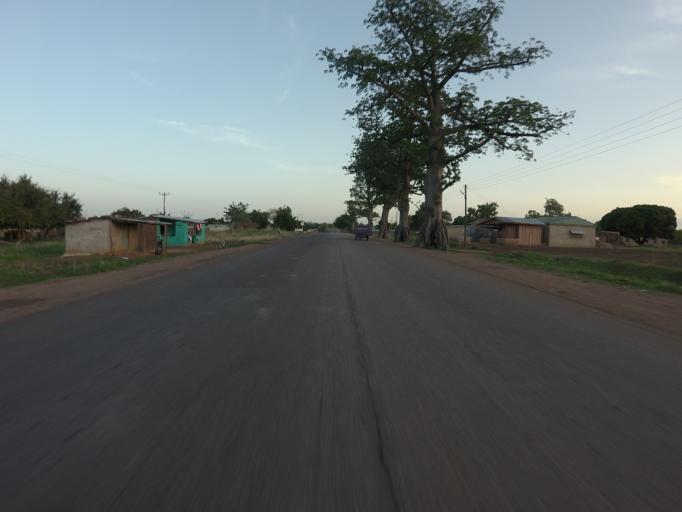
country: GH
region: Upper East
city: Navrongo
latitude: 10.9197
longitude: -1.0895
